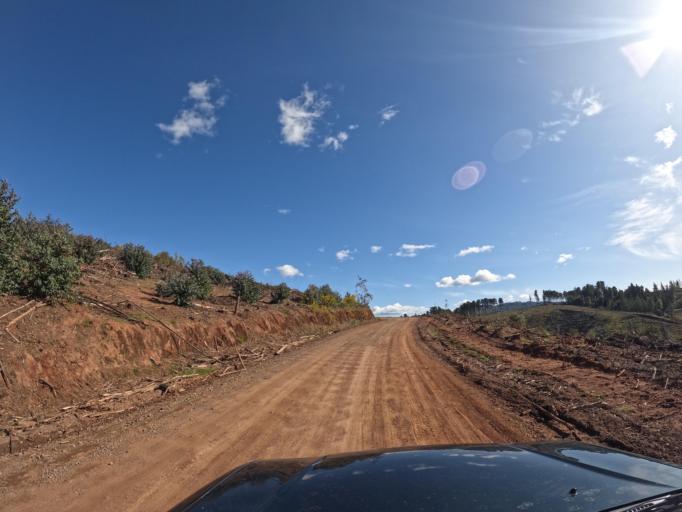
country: CL
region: Biobio
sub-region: Provincia de Biobio
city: La Laja
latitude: -37.0849
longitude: -72.8326
